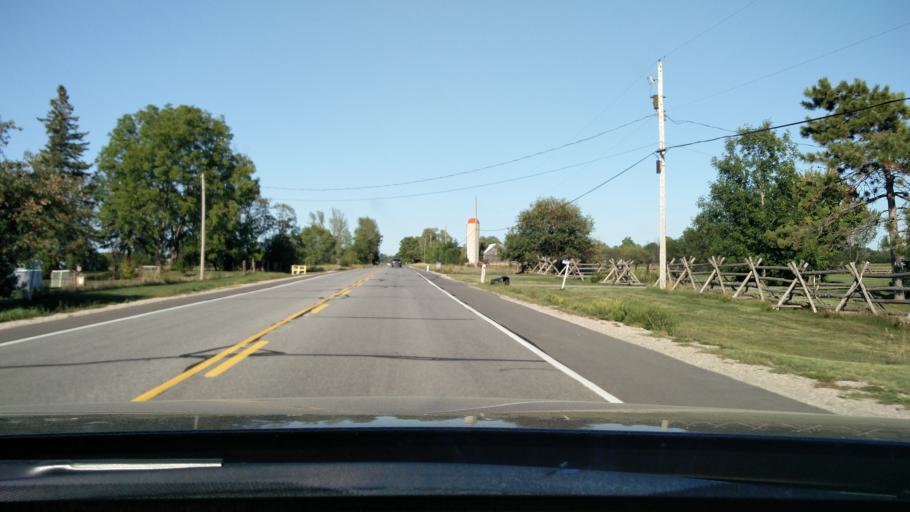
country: CA
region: Ontario
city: Perth
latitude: 44.9514
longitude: -76.1682
